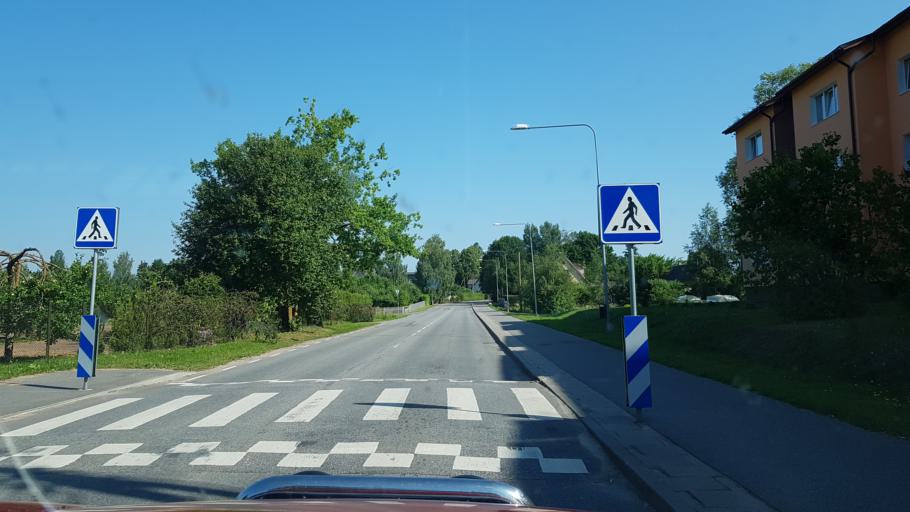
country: EE
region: Tartu
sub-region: Tartu linn
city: Tartu
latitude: 58.4208
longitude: 26.7624
